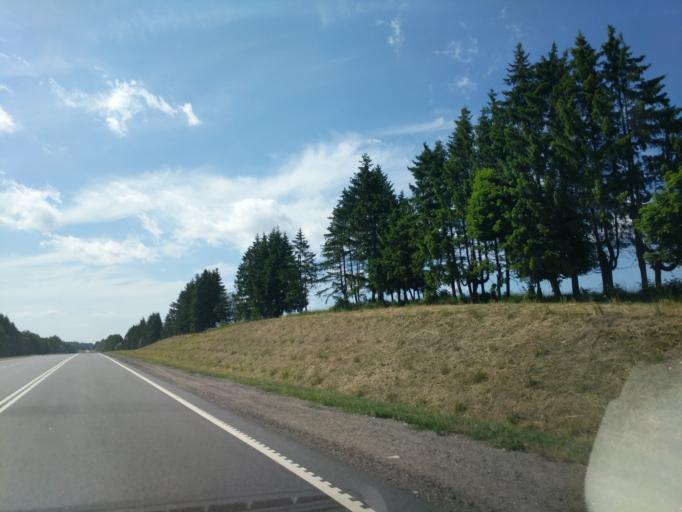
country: BY
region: Minsk
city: Syomkava
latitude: 54.1152
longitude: 27.4299
